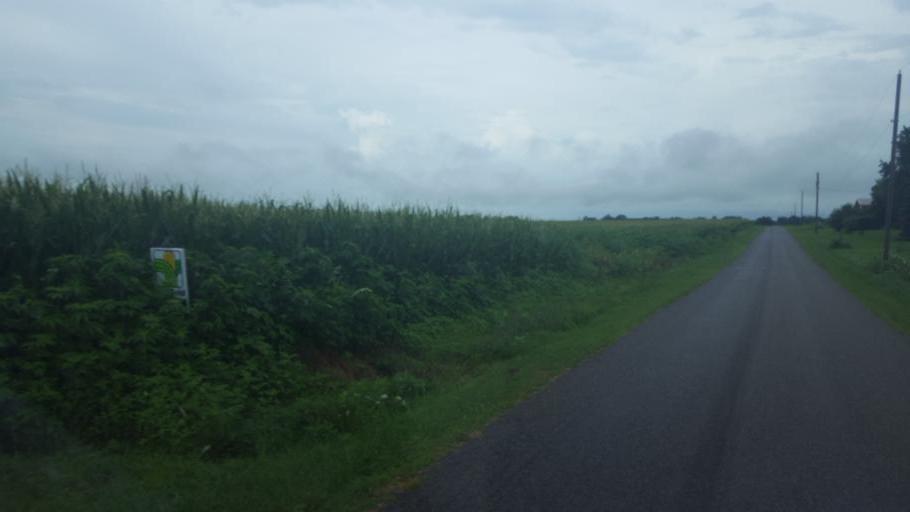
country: US
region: Ohio
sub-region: Union County
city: Richwood
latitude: 40.4962
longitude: -83.2996
